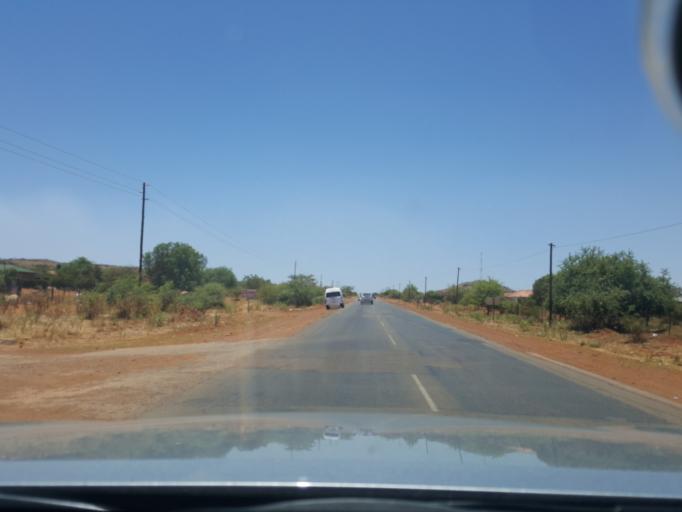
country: ZA
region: North-West
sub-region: Ngaka Modiri Molema District Municipality
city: Zeerust
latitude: -25.4654
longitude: 25.9727
